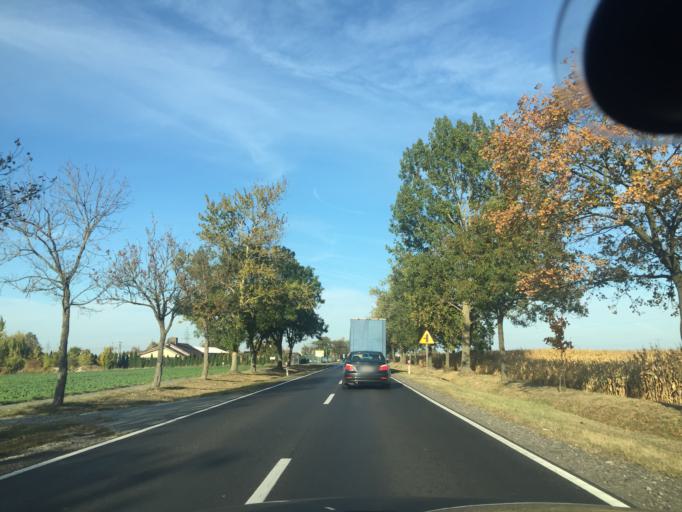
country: PL
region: Kujawsko-Pomorskie
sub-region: Powiat inowroclawski
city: Wierzchoslawice
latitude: 52.8783
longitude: 18.3810
